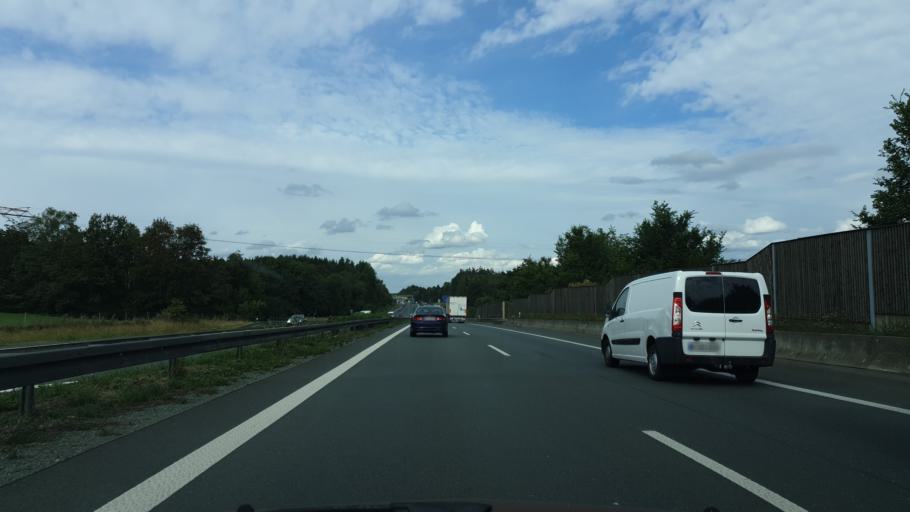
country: DE
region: Saxony
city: Treuen
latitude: 50.5431
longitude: 12.2639
